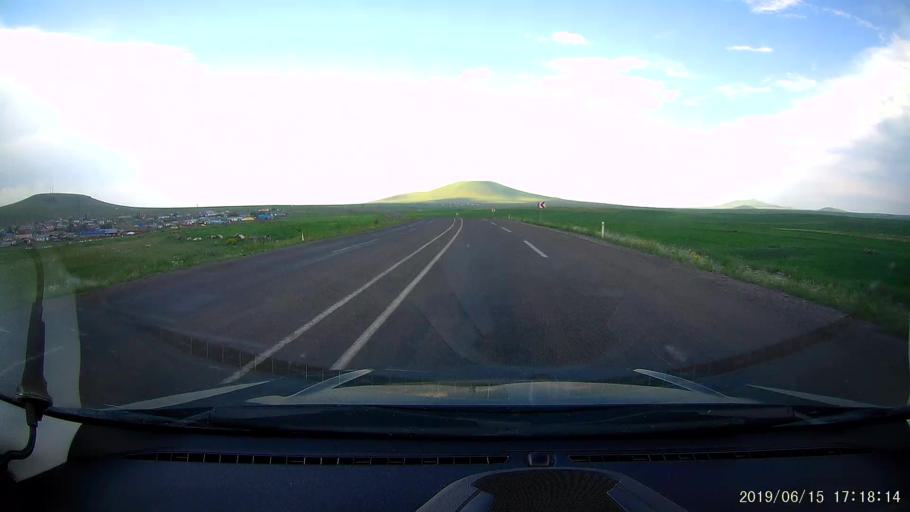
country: TR
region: Kars
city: Kars
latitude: 40.6129
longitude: 43.2537
